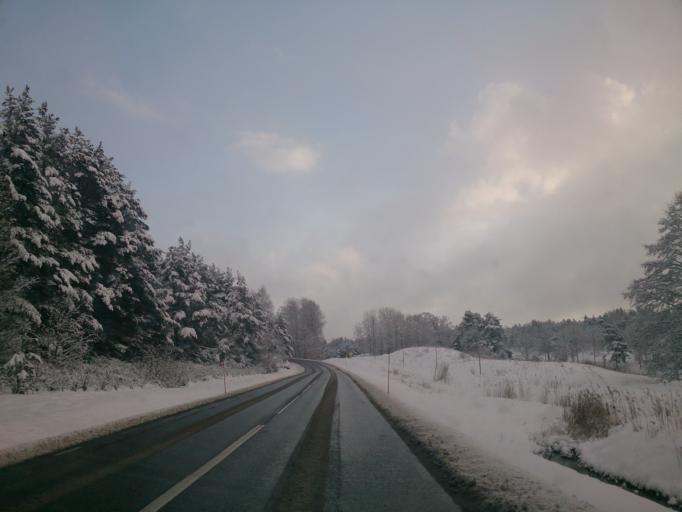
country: SE
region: Stockholm
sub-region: Varmdo Kommun
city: Hemmesta
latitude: 59.3058
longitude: 18.4781
